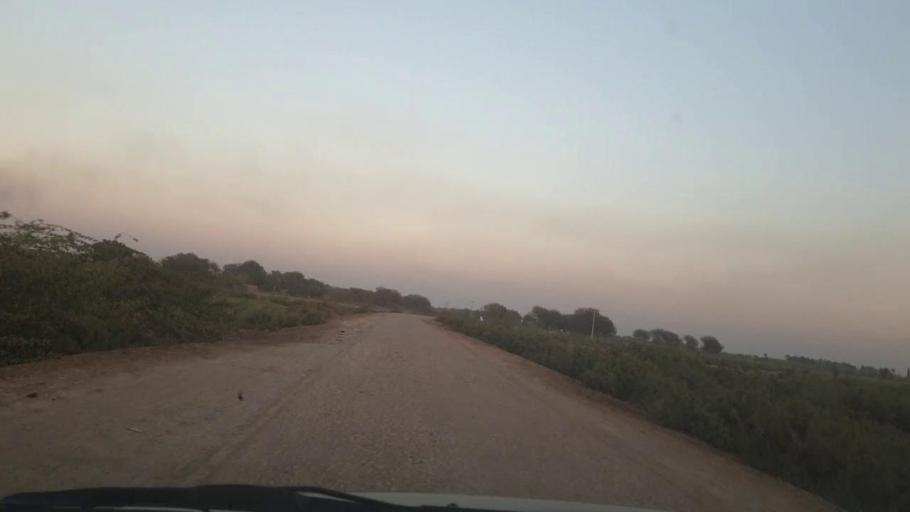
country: PK
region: Sindh
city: Mirpur Khas
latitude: 25.4976
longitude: 69.0378
